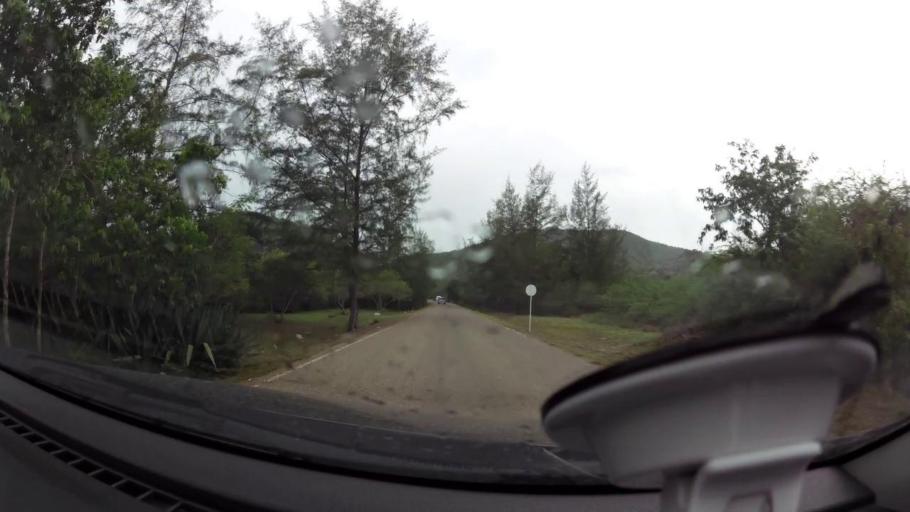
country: TH
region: Prachuap Khiri Khan
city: Pran Buri
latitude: 12.4192
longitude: 99.9832
